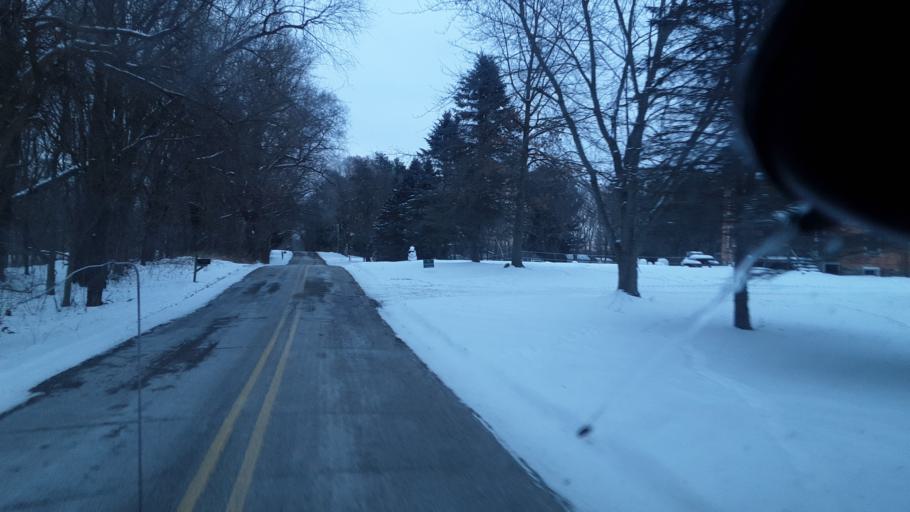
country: US
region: Michigan
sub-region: Ingham County
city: Leslie
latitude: 42.4416
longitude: -84.3435
